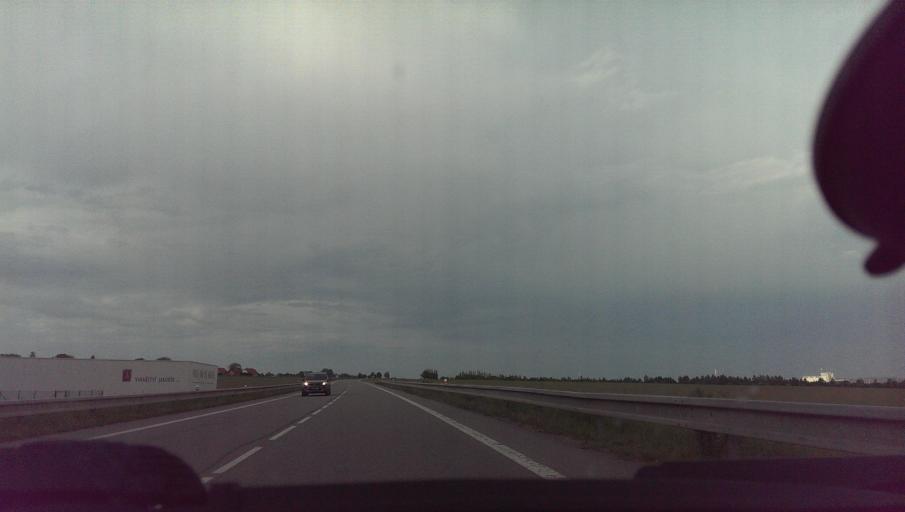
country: CZ
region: Zlin
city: Zlechov
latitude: 49.0694
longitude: 17.3923
